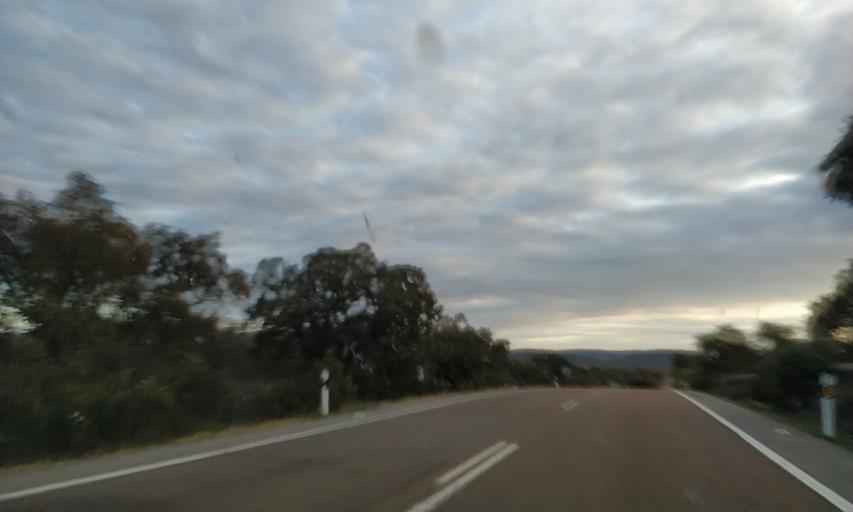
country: ES
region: Extremadura
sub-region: Provincia de Badajoz
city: Puebla de Obando
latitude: 39.2266
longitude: -6.5724
